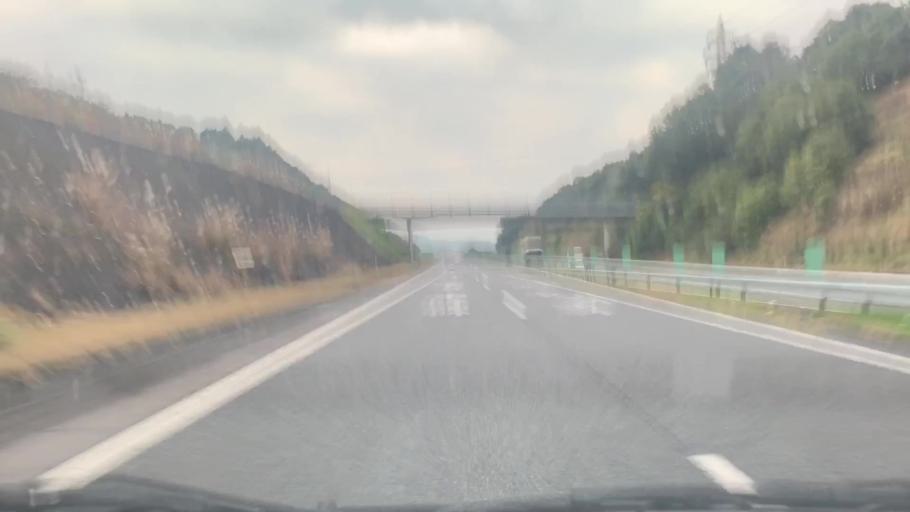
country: JP
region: Nagasaki
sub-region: Isahaya-shi
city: Isahaya
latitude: 32.8221
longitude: 129.9942
